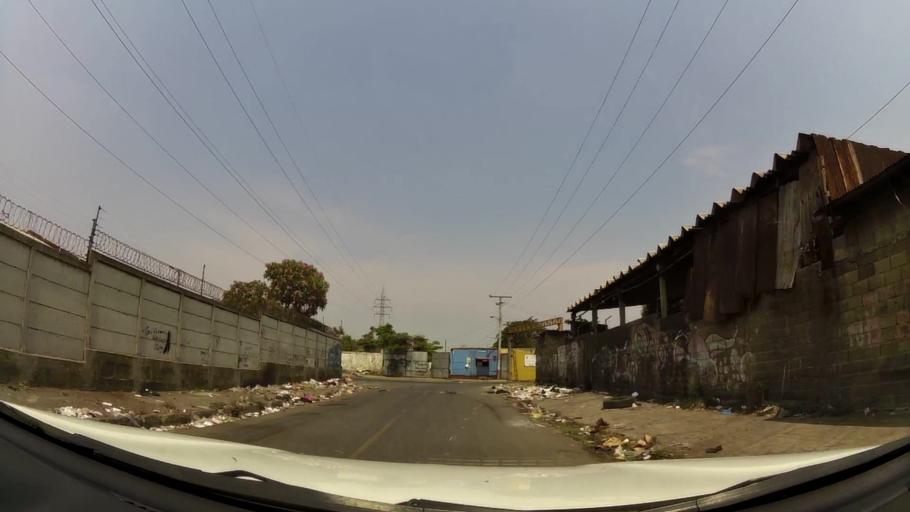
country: NI
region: Managua
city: Ciudad Sandino
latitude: 12.1609
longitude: -86.3001
